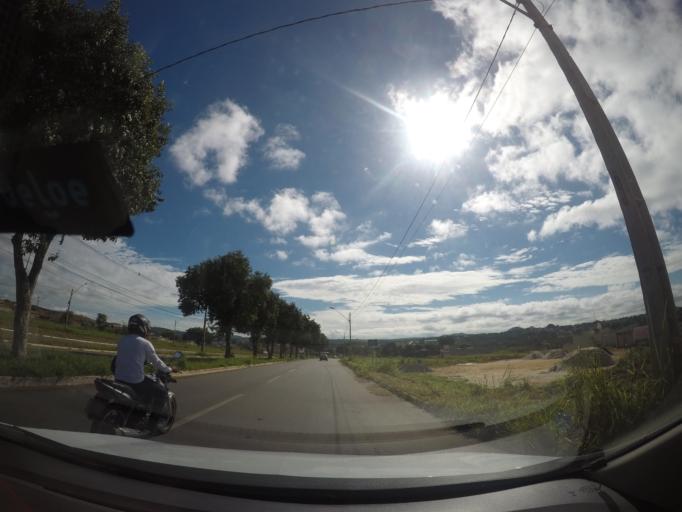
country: BR
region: Goias
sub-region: Goiania
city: Goiania
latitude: -16.6532
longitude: -49.1744
